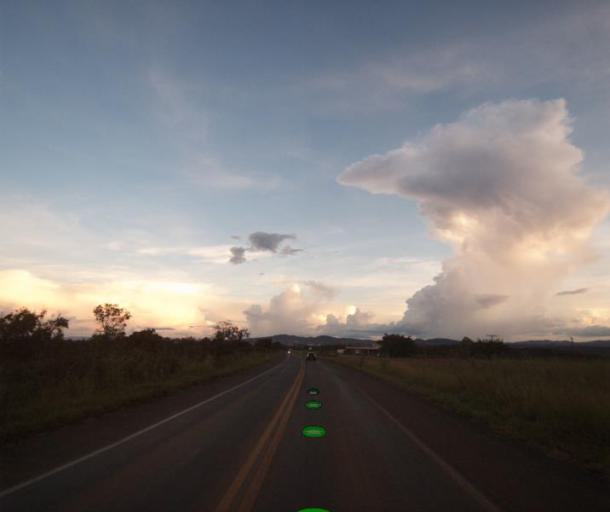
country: BR
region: Goias
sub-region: Uruacu
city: Uruacu
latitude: -14.4737
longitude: -49.1558
